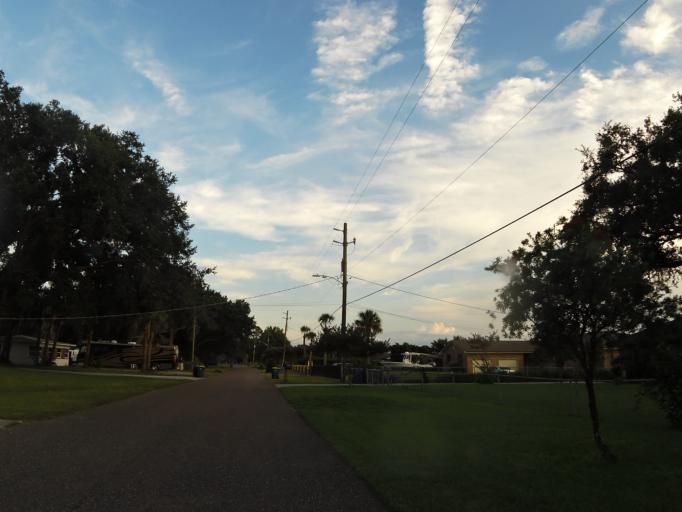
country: US
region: Florida
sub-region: Duval County
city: Atlantic Beach
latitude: 30.3981
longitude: -81.5047
